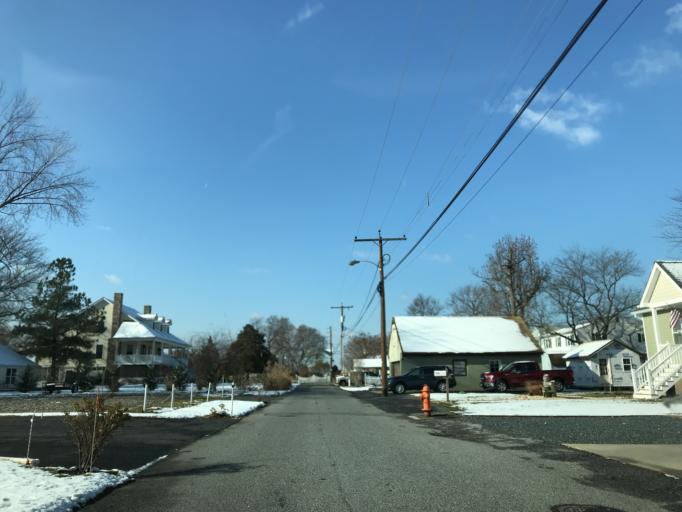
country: US
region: Maryland
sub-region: Baltimore County
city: Bowleys Quarters
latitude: 39.3026
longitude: -76.3815
